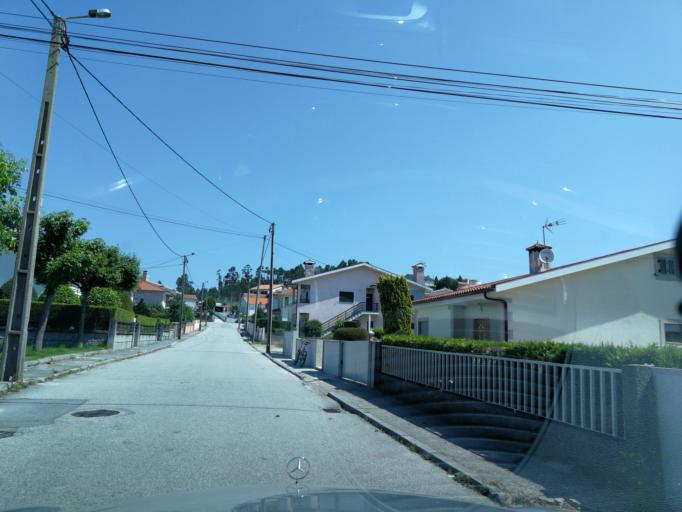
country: PT
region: Braga
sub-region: Braga
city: Adaufe
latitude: 41.5545
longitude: -8.3482
